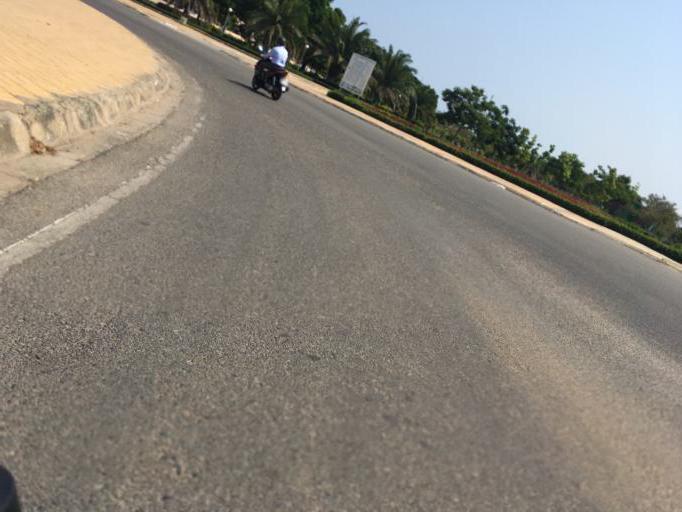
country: VN
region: Ninh Thuan
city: Phan Rang-Thap Cham
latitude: 11.5655
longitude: 108.9984
